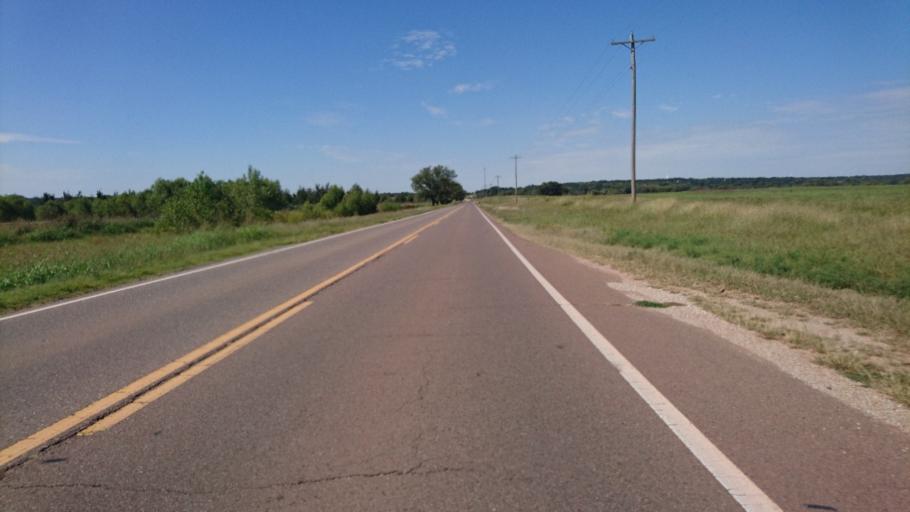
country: US
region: Oklahoma
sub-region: Oklahoma County
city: Jones
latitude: 35.6671
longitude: -97.3020
